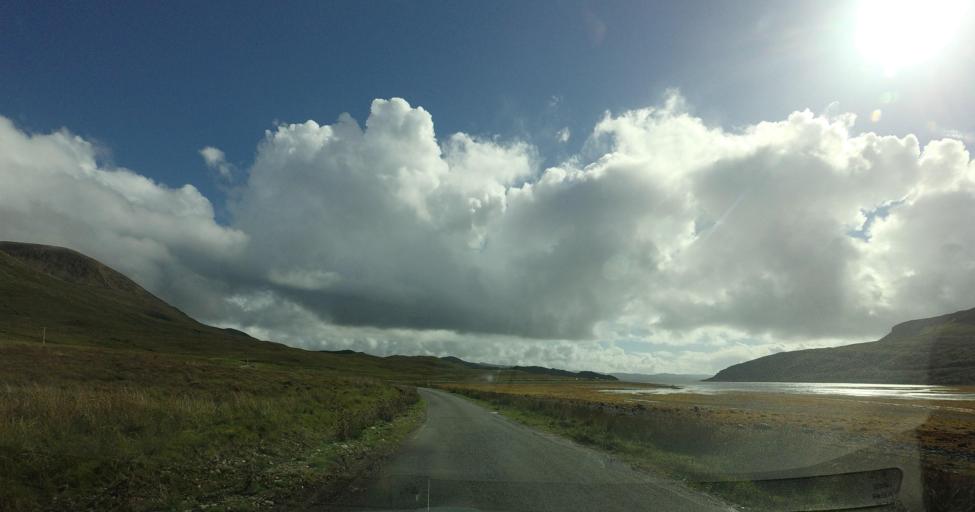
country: GB
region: Scotland
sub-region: Highland
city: Portree
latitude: 57.2260
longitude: -6.0336
